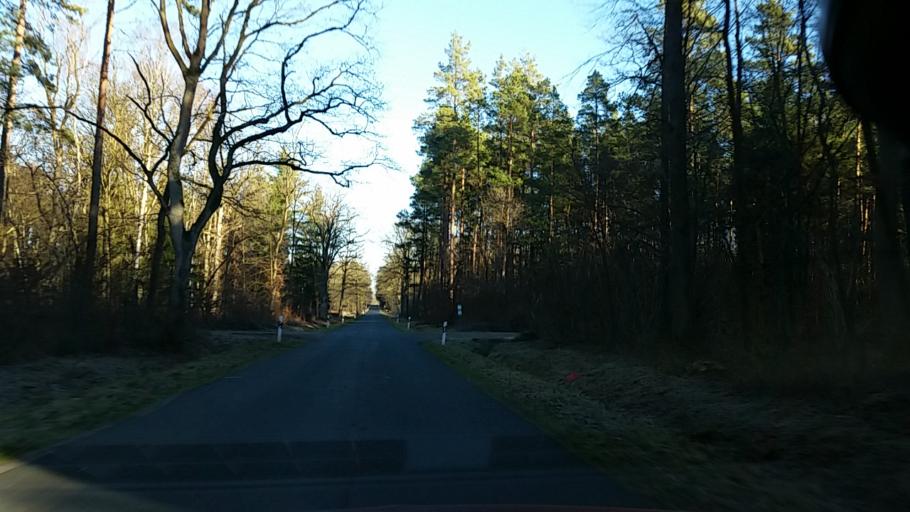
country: DE
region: Lower Saxony
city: Ruhen
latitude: 52.5083
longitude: 10.9075
